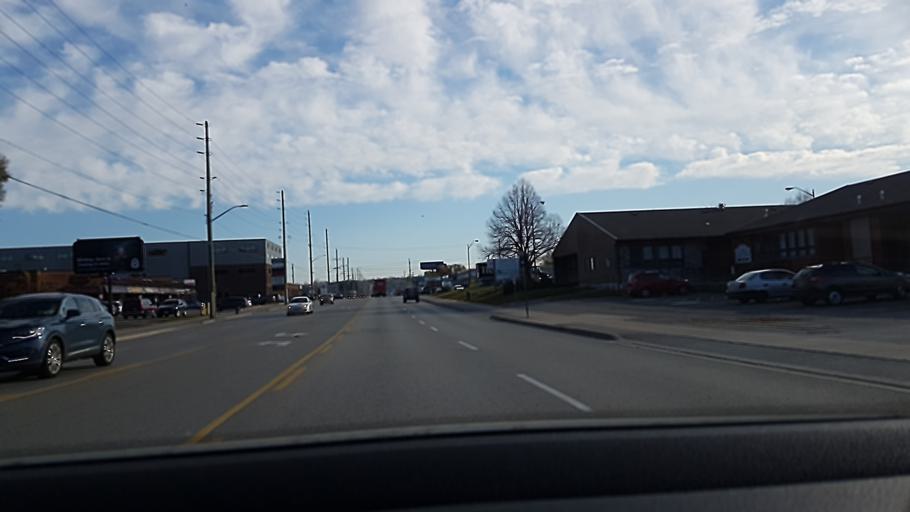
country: CA
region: Ontario
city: Barrie
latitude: 44.3820
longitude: -79.7047
